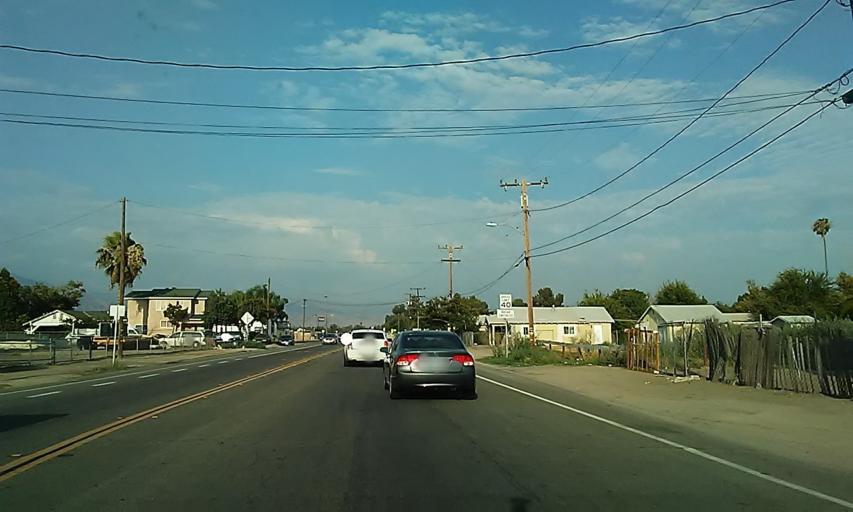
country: US
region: California
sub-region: San Bernardino County
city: San Bernardino
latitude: 34.1083
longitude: -117.2781
